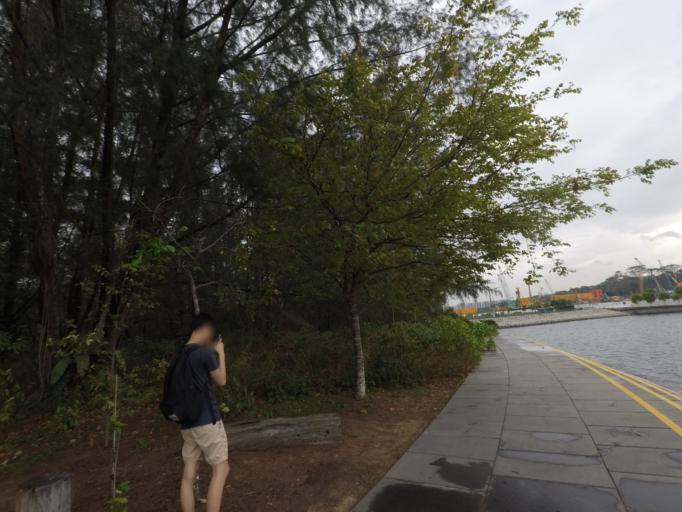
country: MY
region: Johor
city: Kampung Pasir Gudang Baru
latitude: 1.4172
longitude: 103.9154
